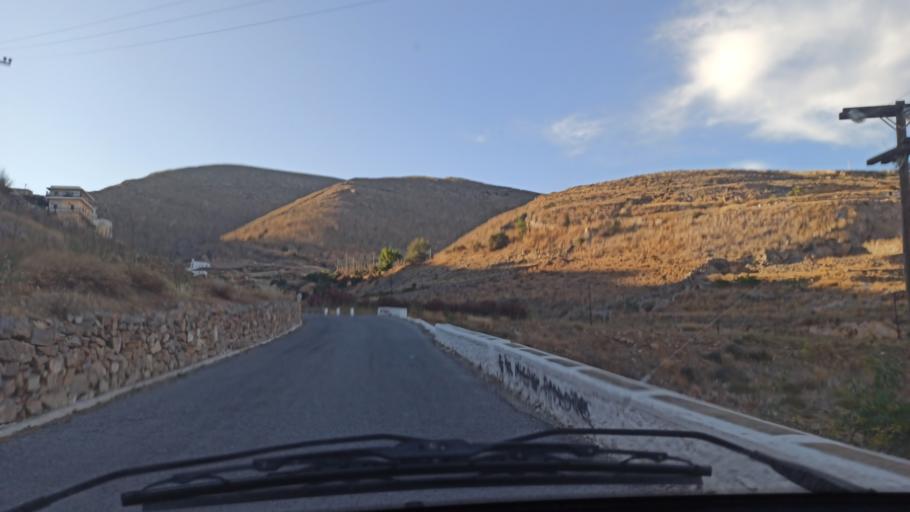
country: GR
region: South Aegean
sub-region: Nomos Kykladon
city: Ano Syros
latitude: 37.4504
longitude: 24.9375
